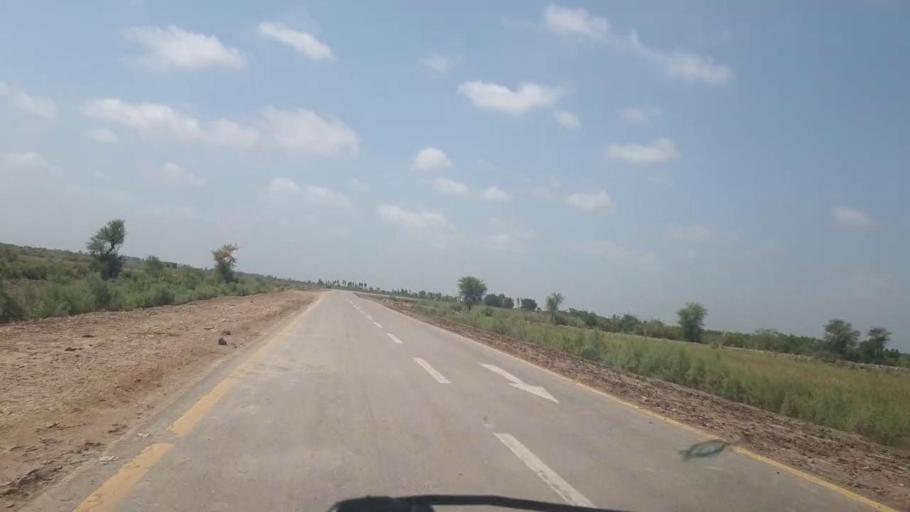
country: PK
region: Sindh
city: Berani
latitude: 25.6954
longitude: 68.9326
